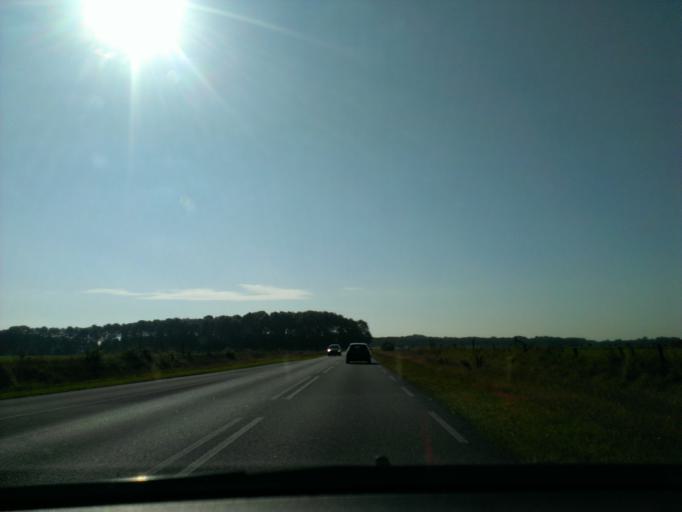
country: NL
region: Drenthe
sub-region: Gemeente Coevorden
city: Dalen
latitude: 52.7143
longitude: 6.7445
